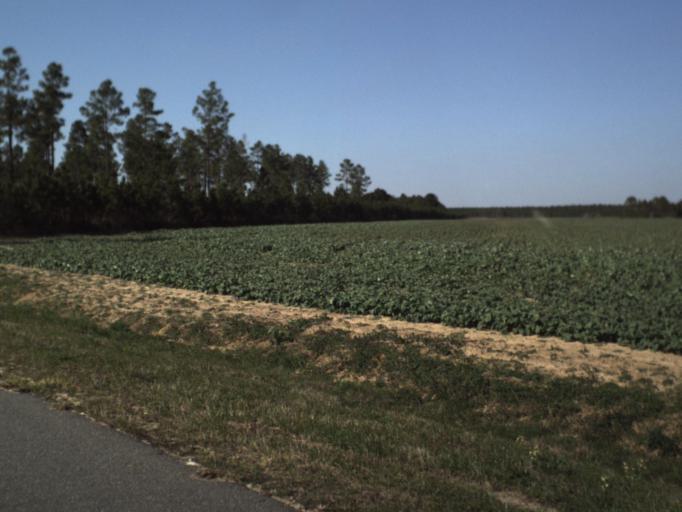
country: US
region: Florida
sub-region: Gulf County
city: Wewahitchka
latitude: 30.2454
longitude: -85.2231
